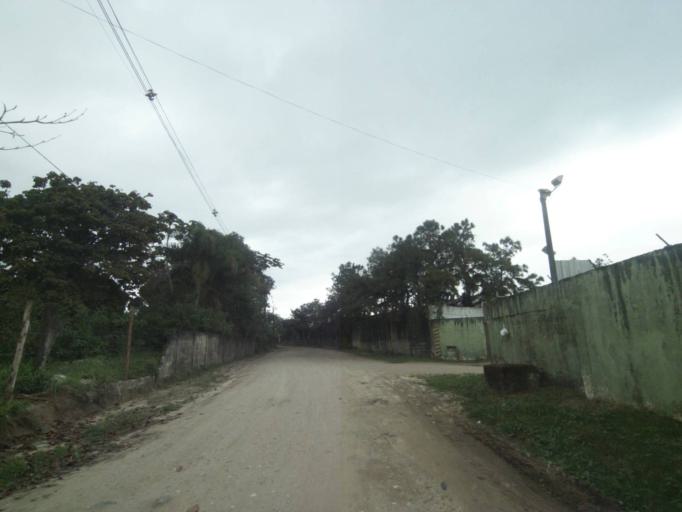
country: BR
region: Parana
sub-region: Paranagua
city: Paranagua
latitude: -25.5424
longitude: -48.5572
